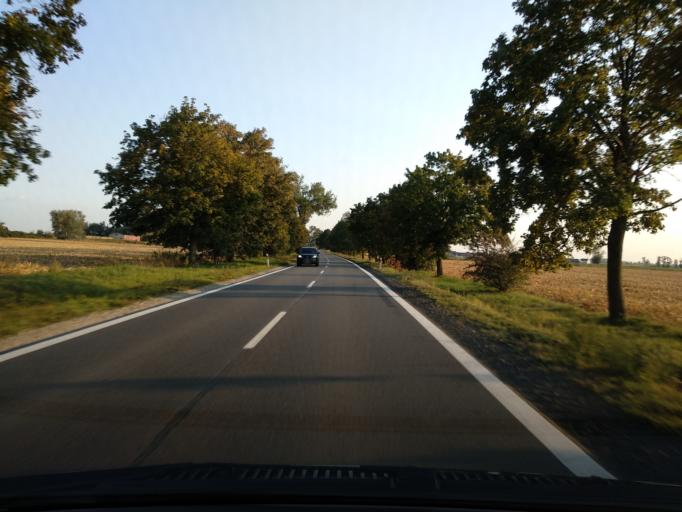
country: PL
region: Lower Silesian Voivodeship
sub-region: Powiat wroclawski
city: Zerniki Wroclawskie
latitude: 51.0049
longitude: 17.0648
